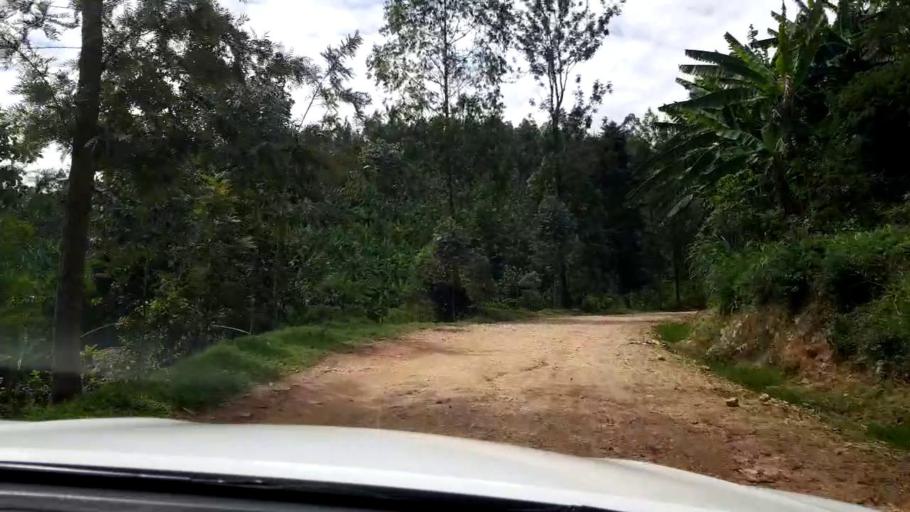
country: RW
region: Southern Province
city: Gitarama
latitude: -1.9277
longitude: 29.6512
